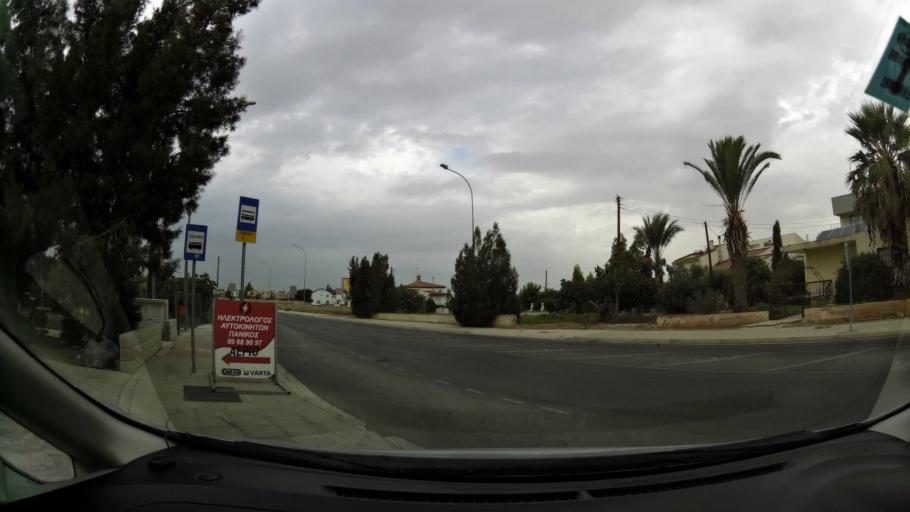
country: CY
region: Lefkosia
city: Geri
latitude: 35.1062
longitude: 33.3965
